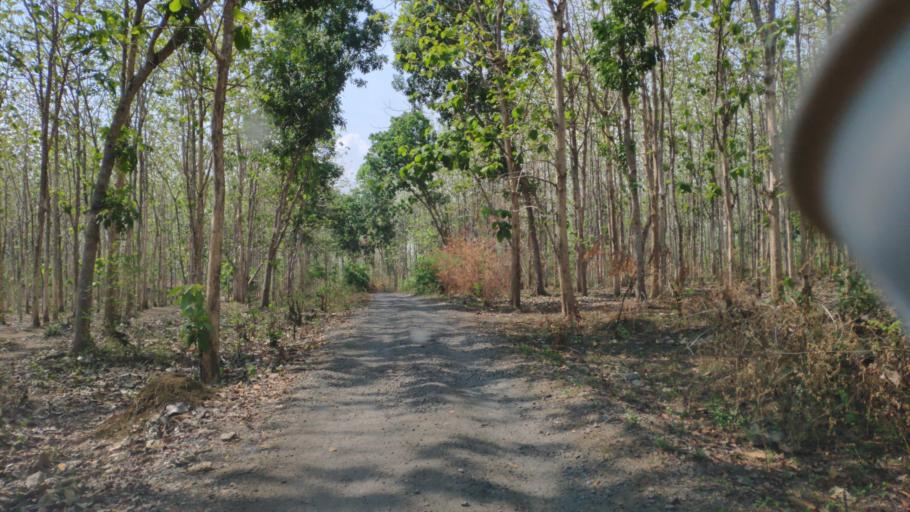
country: ID
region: Central Java
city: Balong Wetan
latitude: -6.9991
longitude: 111.2747
